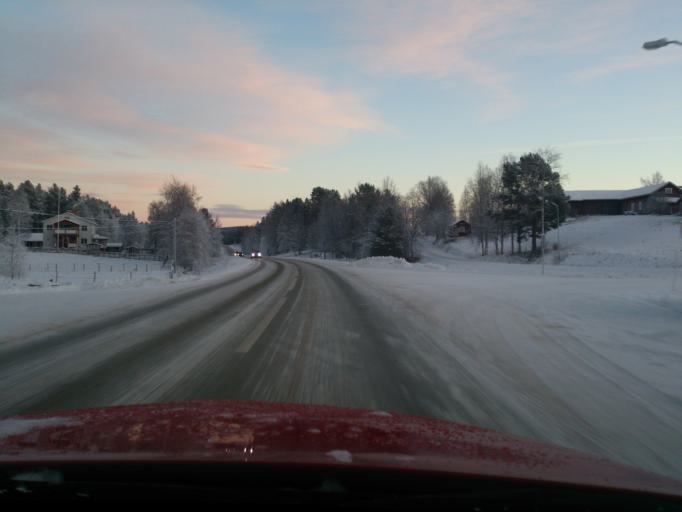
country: SE
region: Jaemtland
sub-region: Harjedalens Kommun
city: Sveg
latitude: 62.4094
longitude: 13.6868
